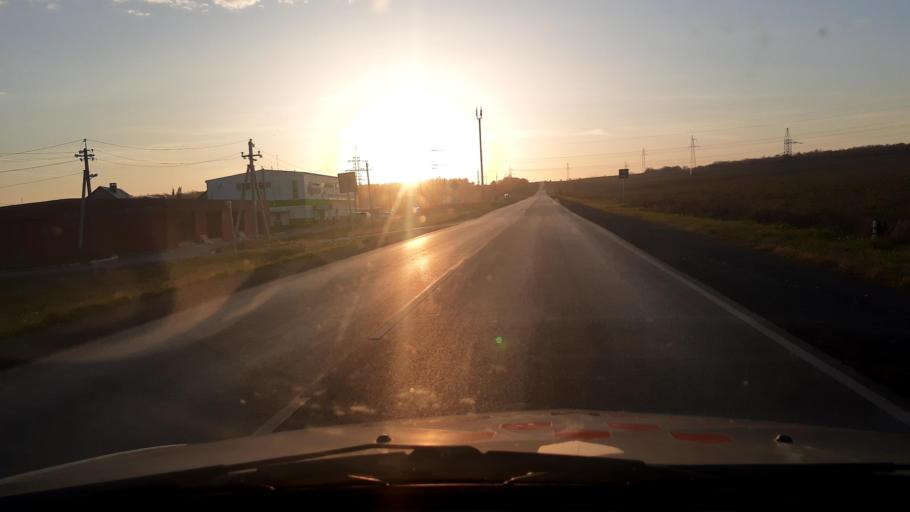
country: RU
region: Bashkortostan
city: Mikhaylovka
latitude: 54.8317
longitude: 55.9086
